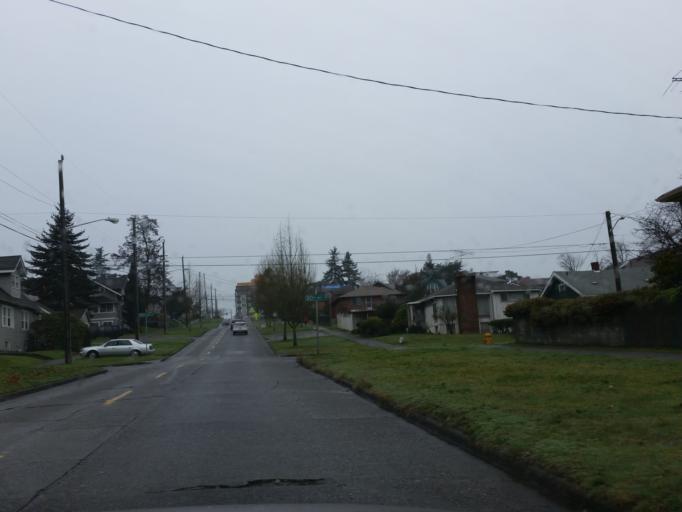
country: US
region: Washington
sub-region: King County
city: Seattle
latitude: 47.5788
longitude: -122.3062
